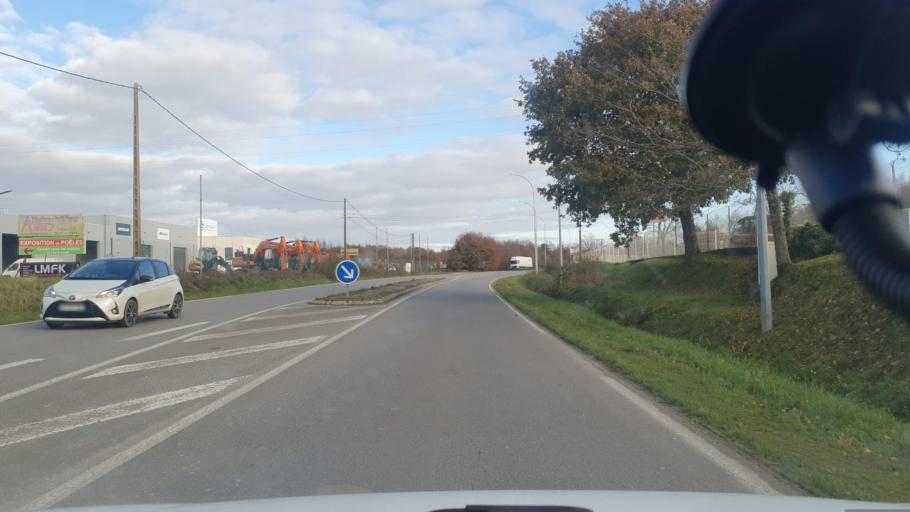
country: FR
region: Brittany
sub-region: Departement du Finistere
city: Briec
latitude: 48.1006
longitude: -4.0268
